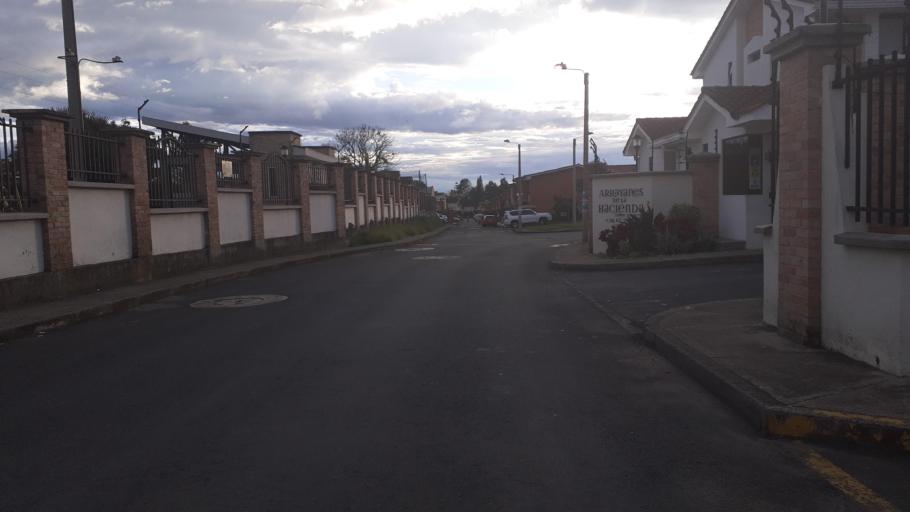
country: CO
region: Cauca
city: Popayan
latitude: 2.4624
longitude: -76.5844
